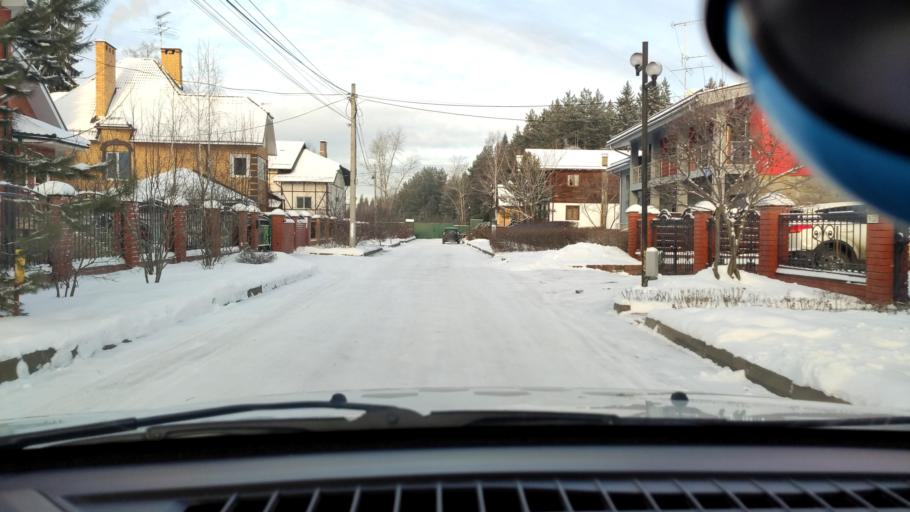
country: RU
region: Perm
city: Kondratovo
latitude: 58.0512
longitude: 56.1015
